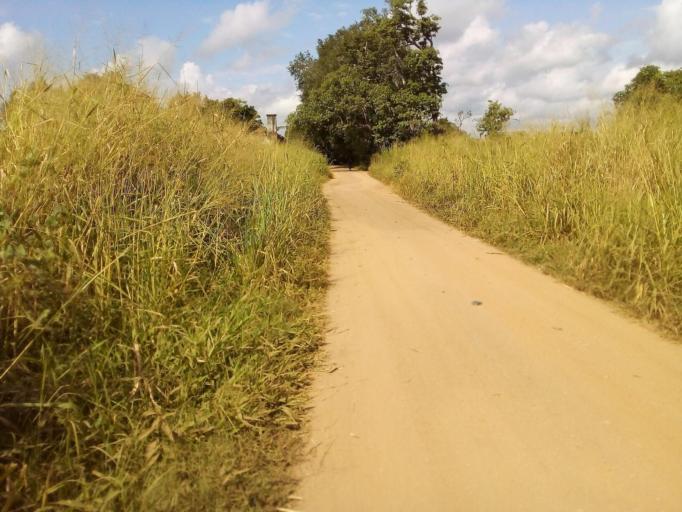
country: MZ
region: Zambezia
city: Quelimane
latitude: -17.5505
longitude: 36.6952
